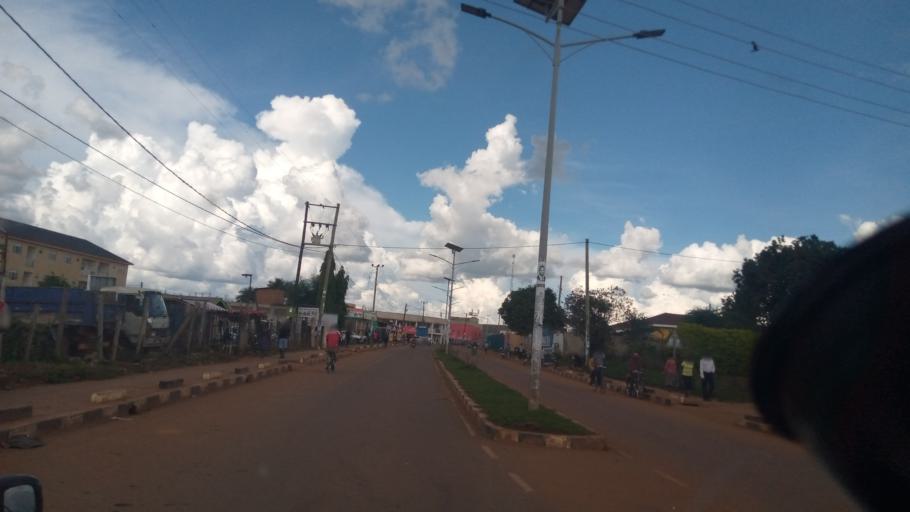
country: UG
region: Northern Region
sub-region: Lira District
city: Lira
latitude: 2.2422
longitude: 32.8927
